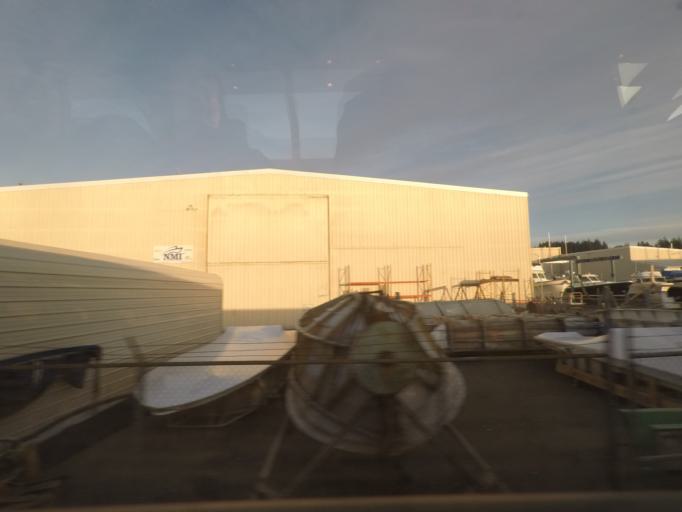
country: US
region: Washington
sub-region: Whatcom County
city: Bellingham
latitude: 48.7222
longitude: -122.5072
